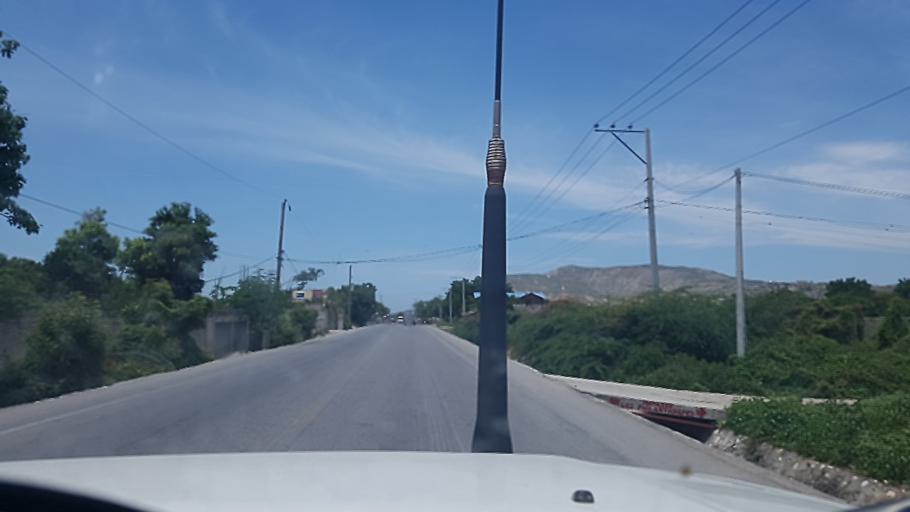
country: HT
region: Artibonite
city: Gonayiv
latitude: 19.4871
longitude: -72.6523
